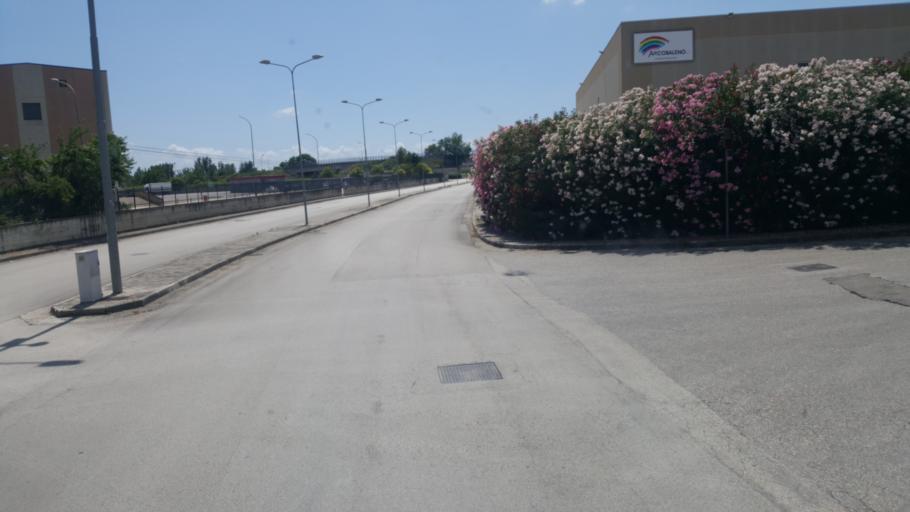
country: IT
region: Campania
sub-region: Provincia di Caserta
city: Maddaloni
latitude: 41.0090
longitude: 14.3652
